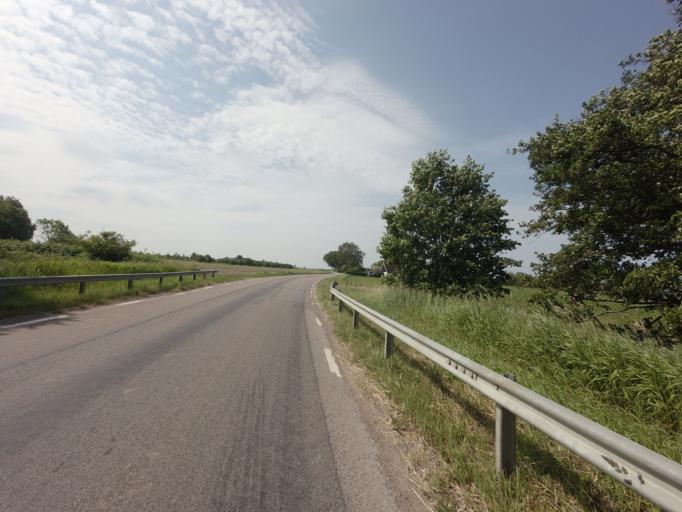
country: SE
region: Skane
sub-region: Helsingborg
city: Odakra
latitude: 56.2016
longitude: 12.7021
